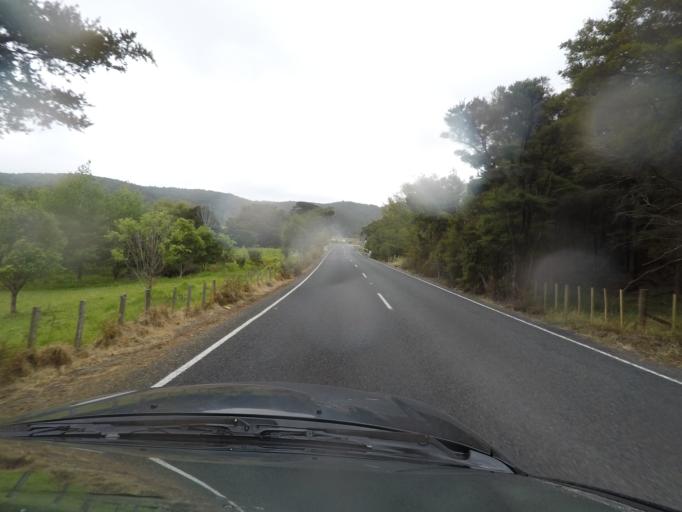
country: NZ
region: Auckland
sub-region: Auckland
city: Warkworth
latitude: -36.2631
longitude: 174.7061
